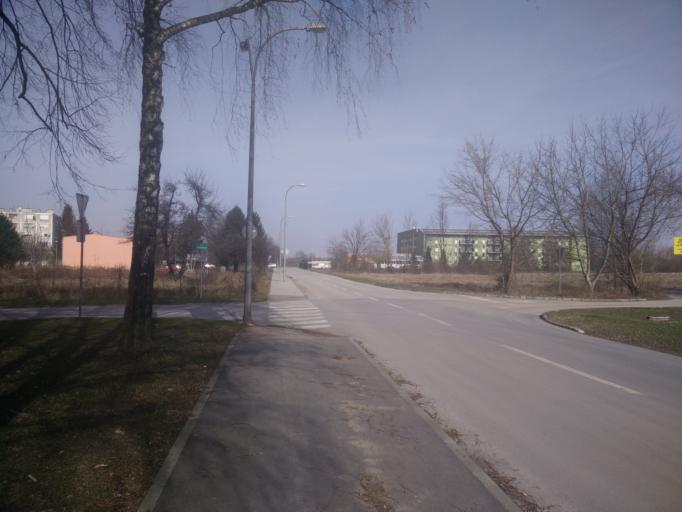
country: HR
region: Karlovacka
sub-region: Grad Karlovac
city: Karlovac
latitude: 45.5002
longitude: 15.5609
